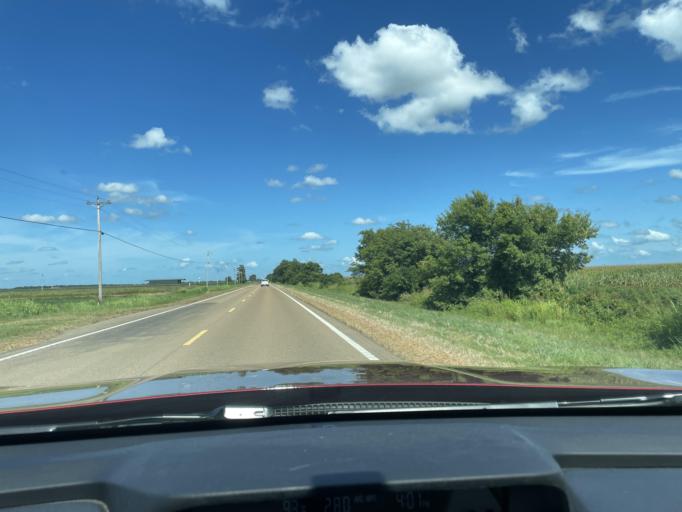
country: US
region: Mississippi
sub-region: Humphreys County
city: Belzoni
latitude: 33.1837
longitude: -90.5391
